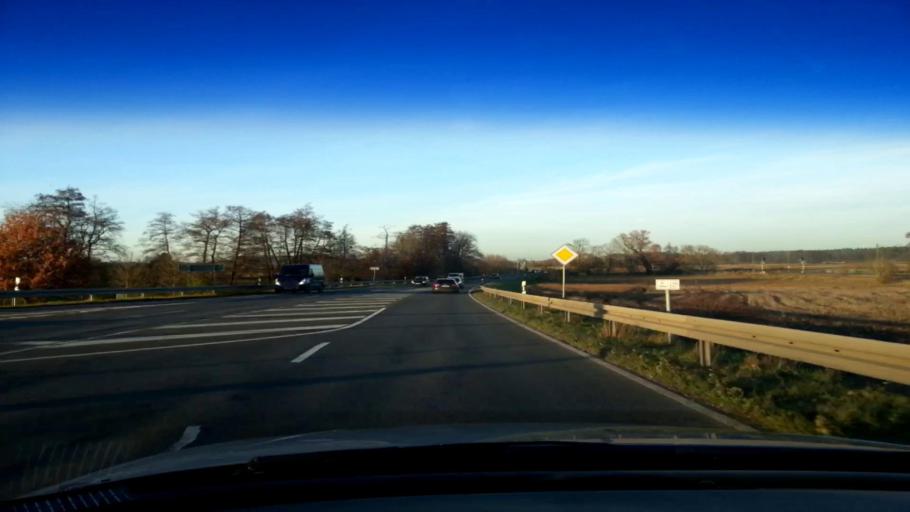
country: DE
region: Bavaria
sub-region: Upper Franconia
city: Hallstadt
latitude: 49.9376
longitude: 10.8845
